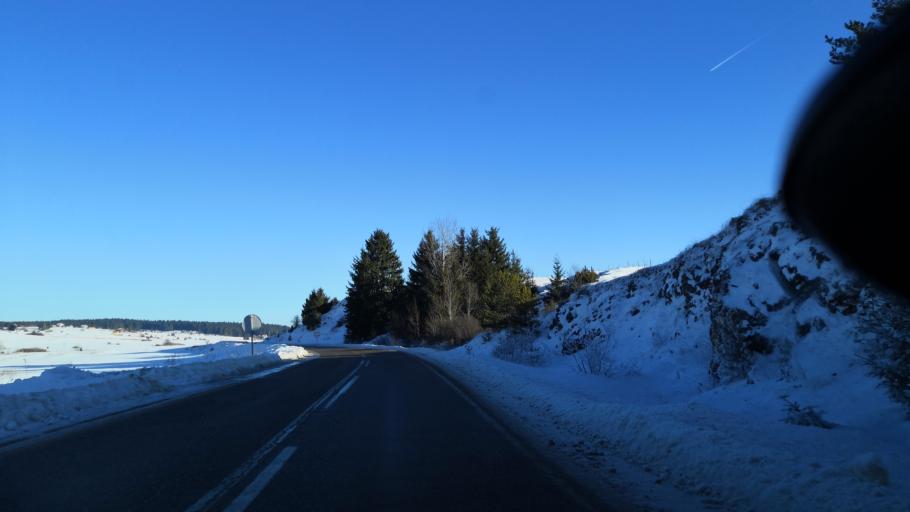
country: BA
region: Republika Srpska
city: Han Pijesak
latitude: 44.0338
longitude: 18.9089
